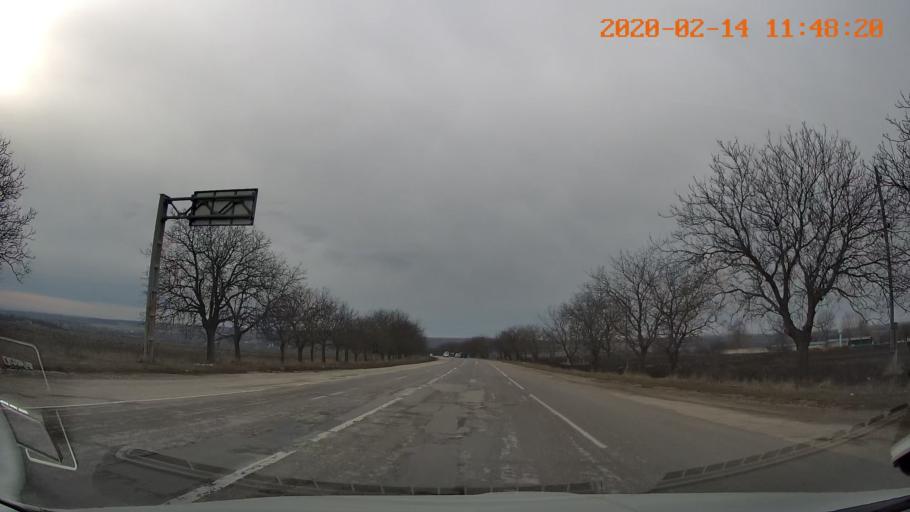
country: MD
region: Briceni
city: Briceni
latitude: 48.3091
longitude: 26.9525
